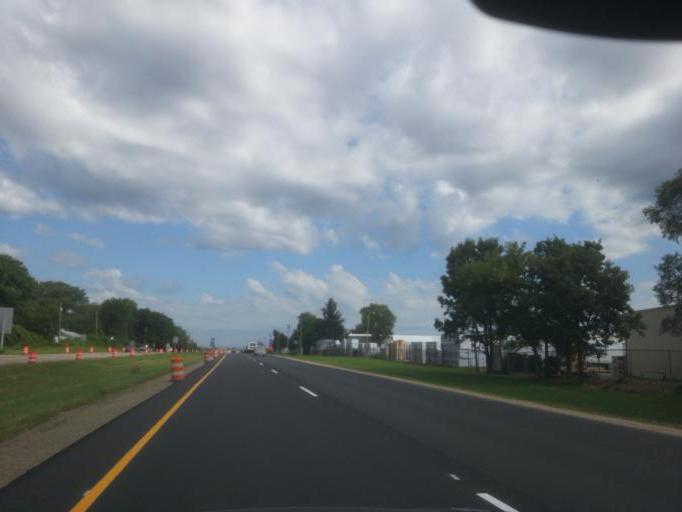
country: US
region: Wisconsin
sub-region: Dane County
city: Monona
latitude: 43.0904
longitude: -89.3136
